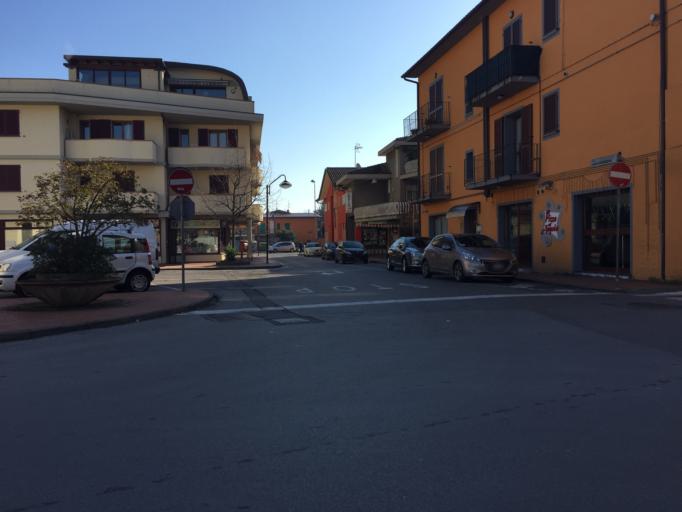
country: IT
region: Tuscany
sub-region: Provincia di Pistoia
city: Ponte Buggianese
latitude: 43.8424
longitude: 10.7479
